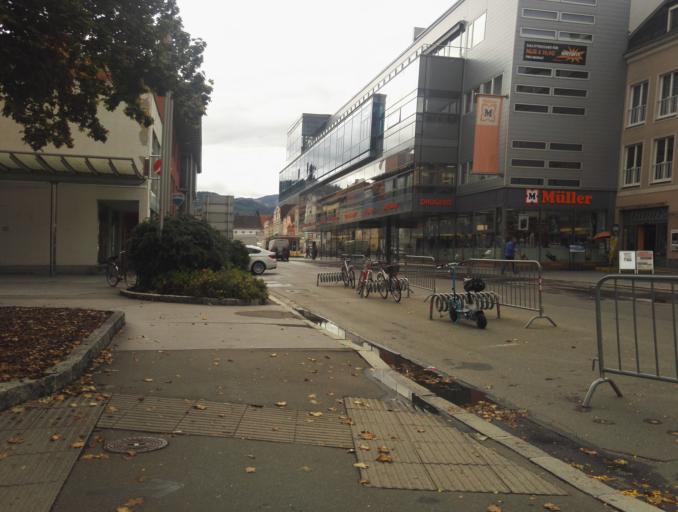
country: AT
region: Styria
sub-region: Politischer Bezirk Leoben
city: Leoben
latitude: 47.3820
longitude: 15.0940
